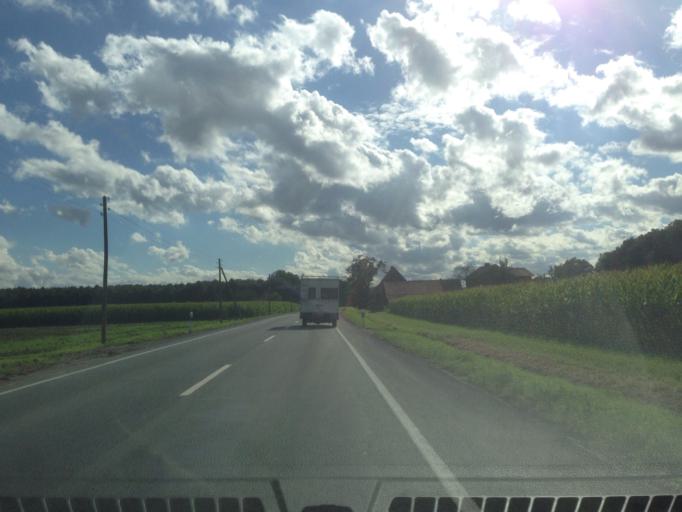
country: DE
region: North Rhine-Westphalia
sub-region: Regierungsbezirk Munster
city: Senden
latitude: 51.8497
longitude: 7.5458
